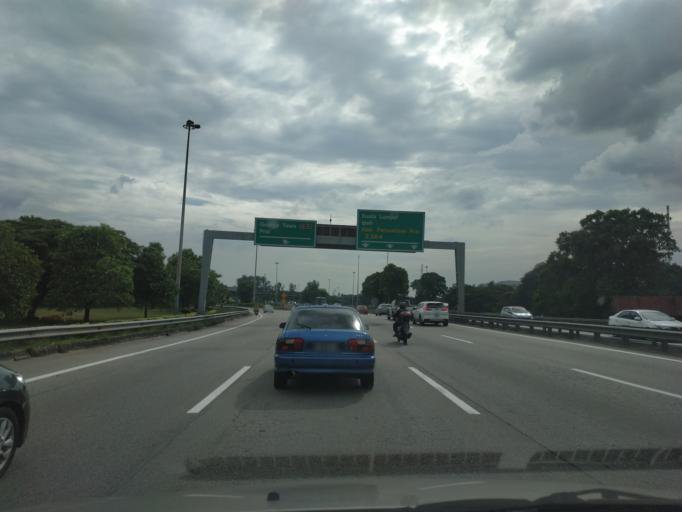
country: MY
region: Penang
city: Perai
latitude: 5.3701
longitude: 100.3999
